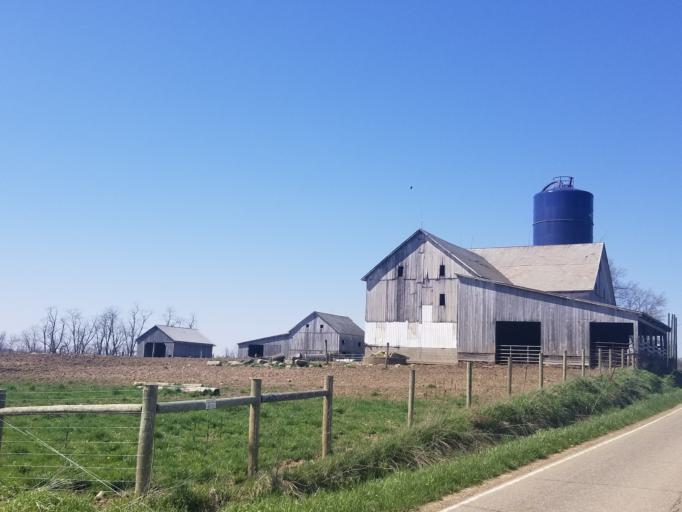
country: US
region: Ohio
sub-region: Knox County
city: Oak Hill
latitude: 40.3228
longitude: -82.1794
